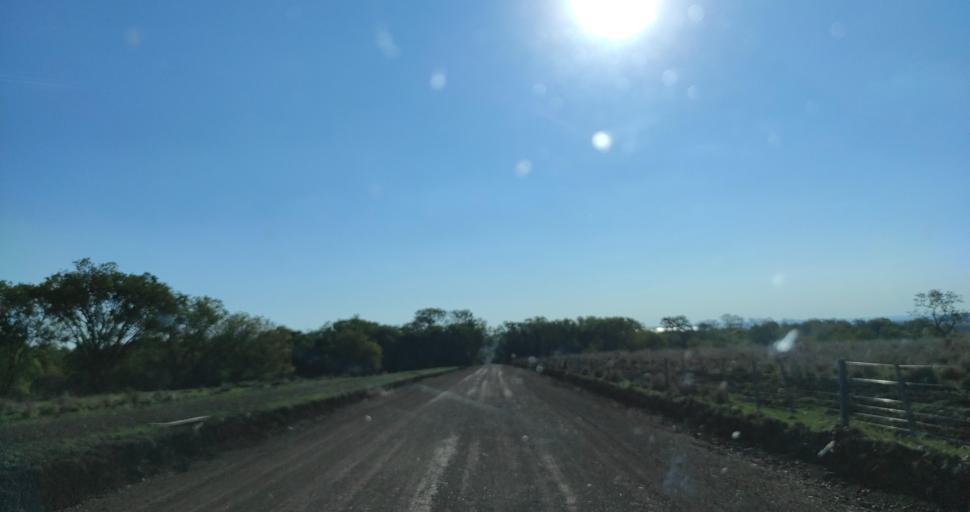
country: PY
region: Itapua
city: San Juan del Parana
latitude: -27.4206
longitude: -56.1200
